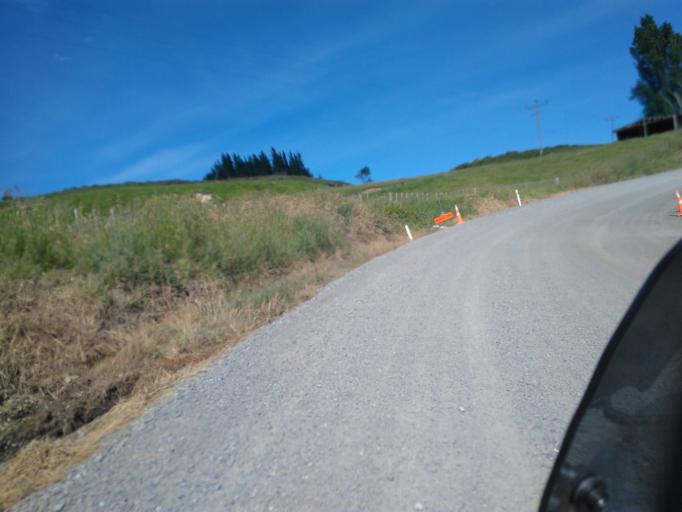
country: NZ
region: Hawke's Bay
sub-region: Wairoa District
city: Wairoa
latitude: -38.8717
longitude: 177.2102
